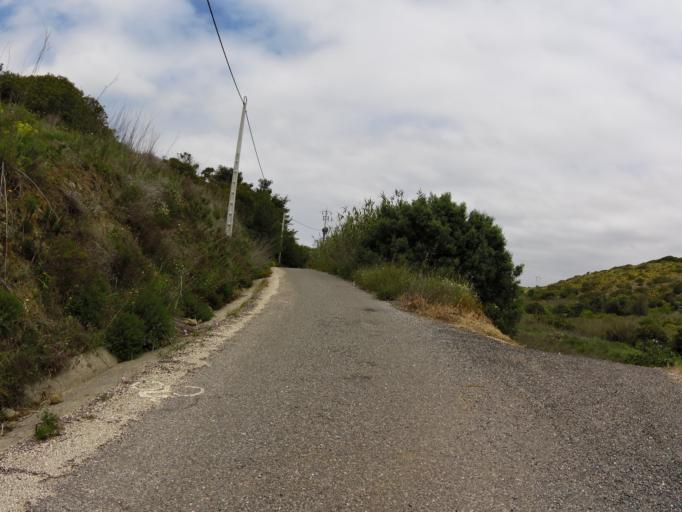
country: PT
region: Faro
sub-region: Vila do Bispo
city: Vila do Bispo
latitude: 37.0757
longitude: -8.8755
